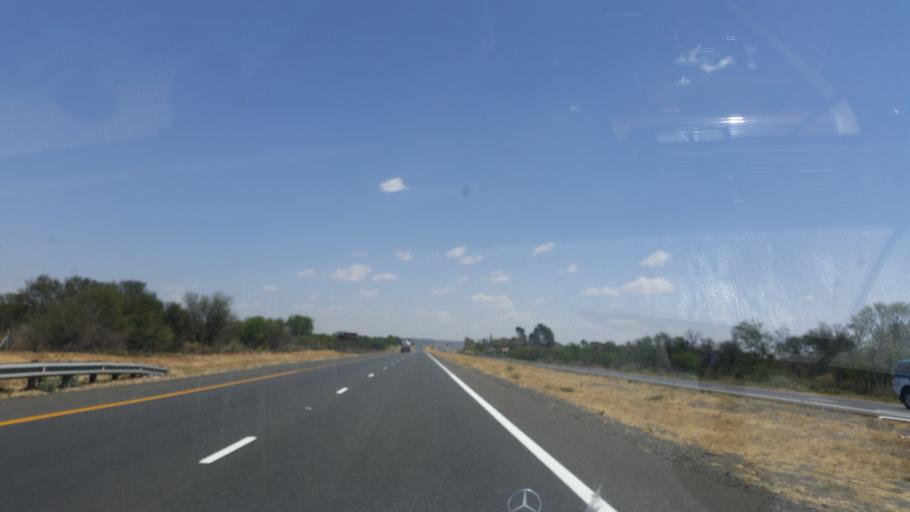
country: ZA
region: Orange Free State
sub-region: Mangaung Metropolitan Municipality
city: Bloemfontein
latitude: -28.9625
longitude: 26.3578
